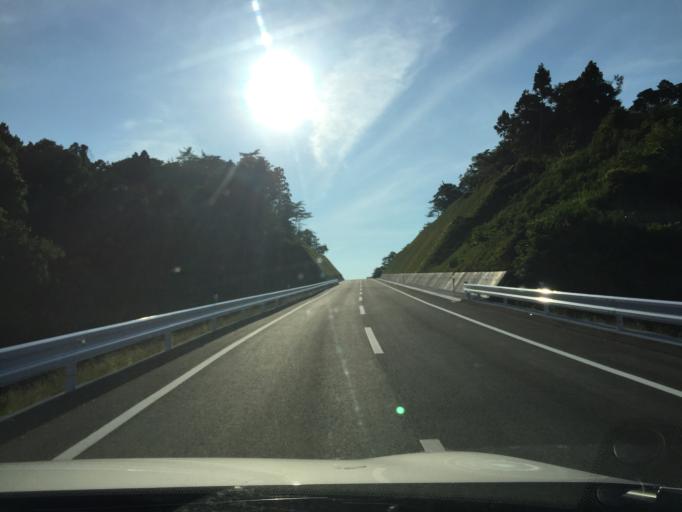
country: JP
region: Fukushima
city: Iwaki
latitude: 37.0001
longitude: 140.9726
